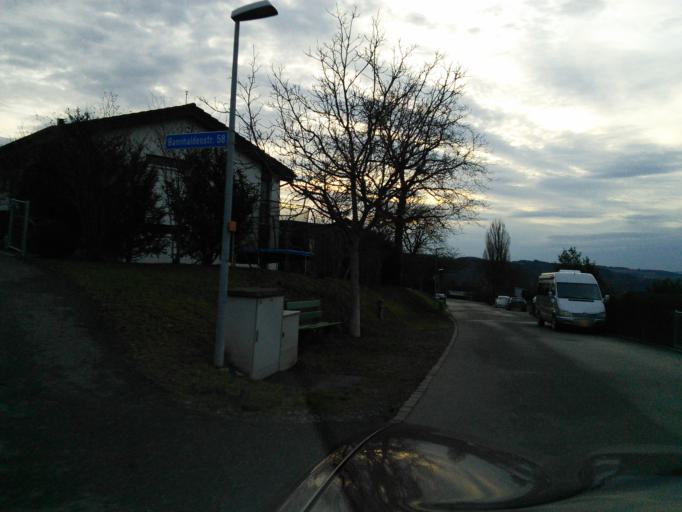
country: CH
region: Thurgau
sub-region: Frauenfeld District
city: Frauenfeld
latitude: 47.5584
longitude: 8.9189
